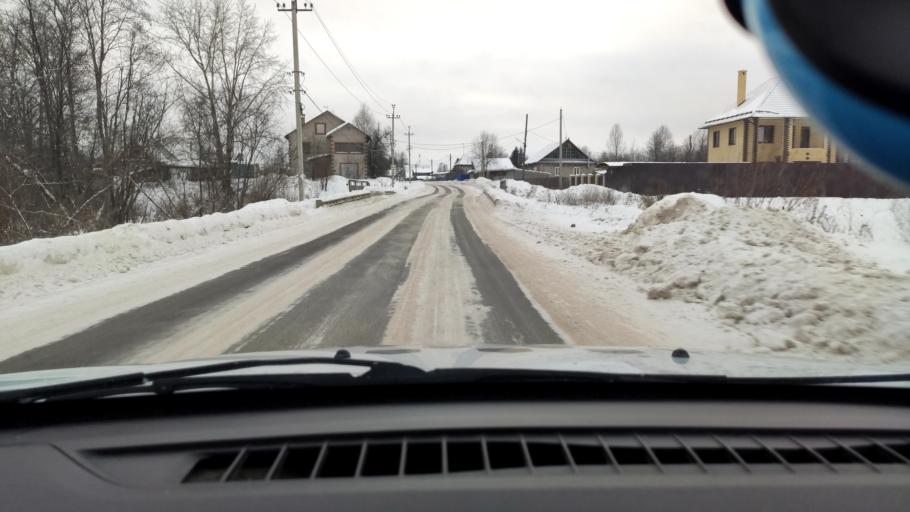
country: RU
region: Perm
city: Overyata
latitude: 58.0772
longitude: 55.9662
